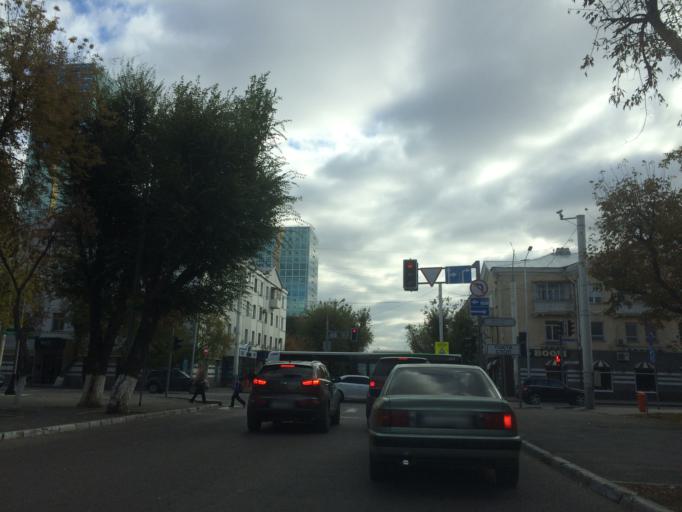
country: KZ
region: Astana Qalasy
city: Astana
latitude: 51.1645
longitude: 71.4170
